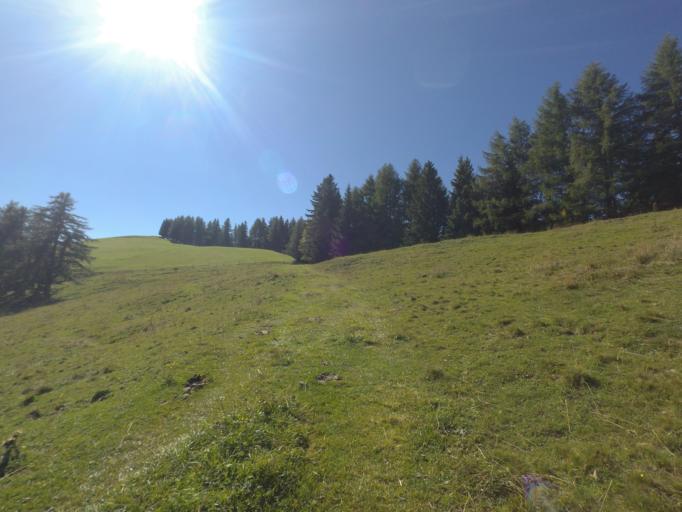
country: AT
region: Styria
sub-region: Politischer Bezirk Weiz
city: Passail
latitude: 47.3363
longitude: 15.4642
